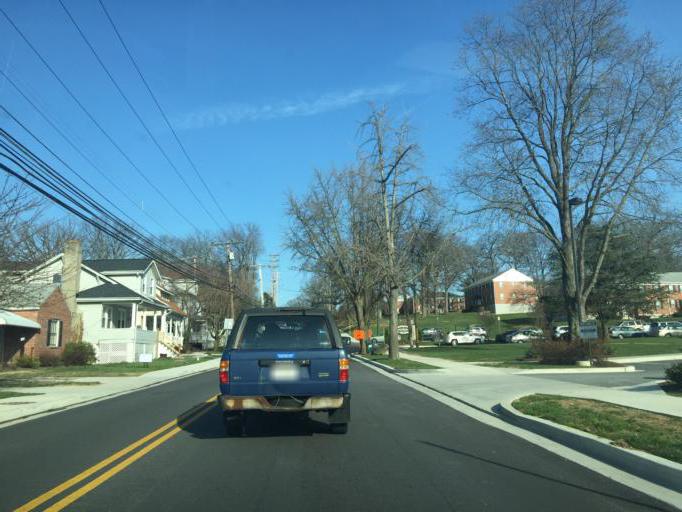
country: US
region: Maryland
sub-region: Baltimore County
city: Towson
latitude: 39.3946
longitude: -76.5952
